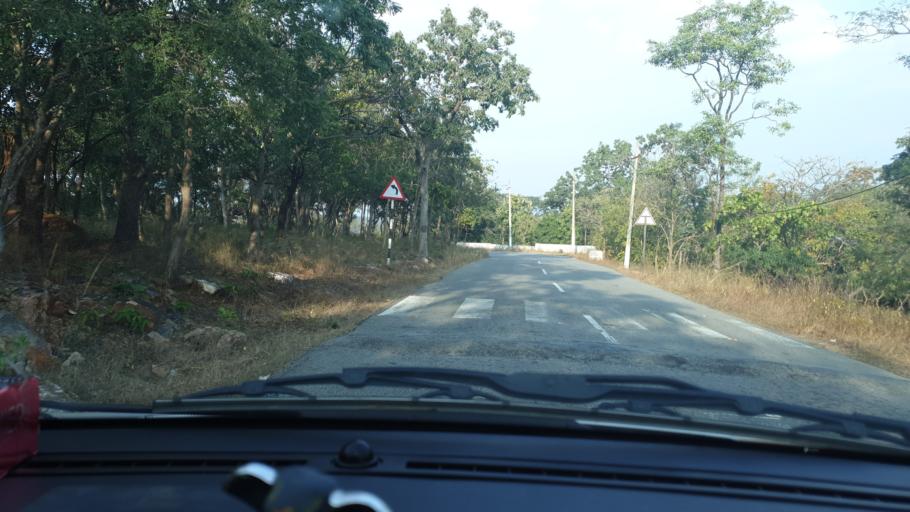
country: IN
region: Andhra Pradesh
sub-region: Kurnool
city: Srisailam
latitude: 16.3060
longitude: 78.7326
